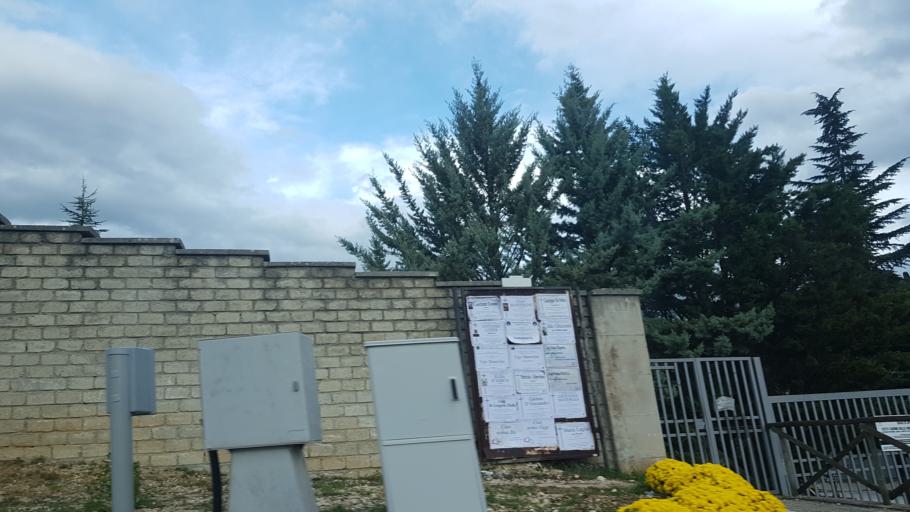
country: IT
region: Abruzzo
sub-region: Provincia dell' Aquila
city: L'Aquila
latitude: 42.3499
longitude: 13.4113
